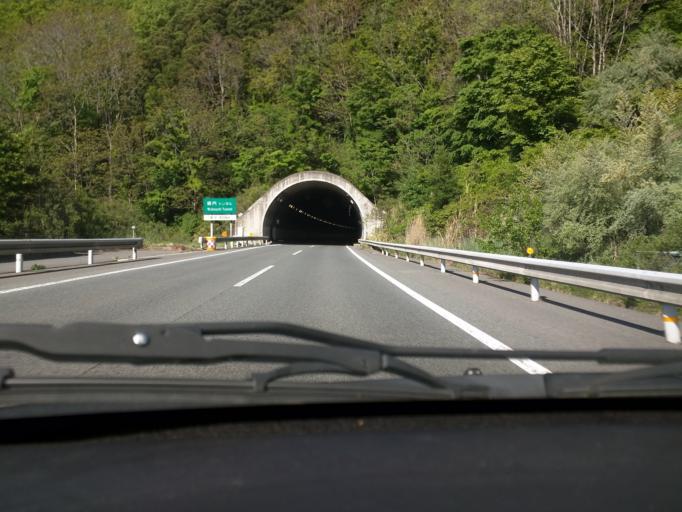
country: JP
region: Nagano
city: Suzaka
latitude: 36.6157
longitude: 138.2597
